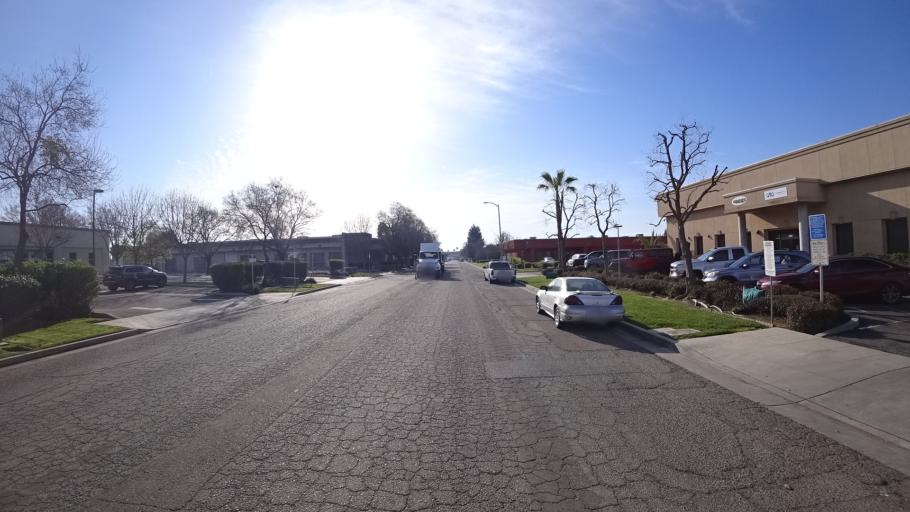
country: US
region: California
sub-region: Fresno County
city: West Park
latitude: 36.8127
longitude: -119.8773
